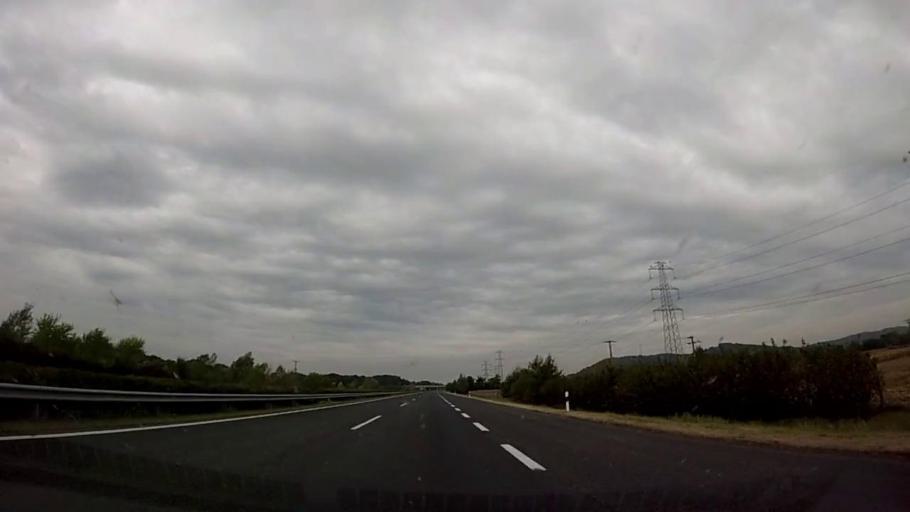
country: HR
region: Medimurska
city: Podturen
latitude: 46.5106
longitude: 16.5546
